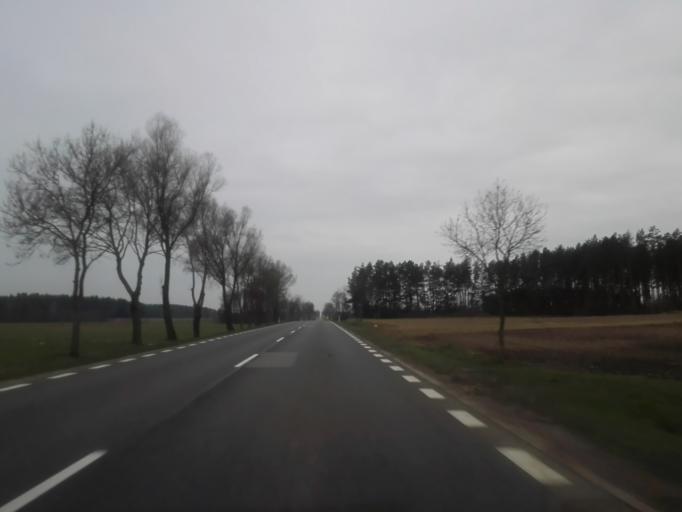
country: PL
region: Podlasie
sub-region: Powiat kolnenski
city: Stawiski
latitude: 53.4725
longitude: 22.2068
